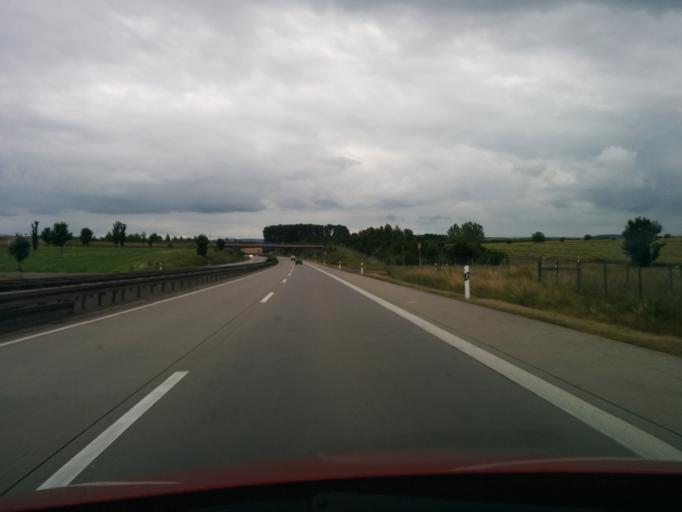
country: DE
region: Thuringia
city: Ingersleben
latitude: 50.9054
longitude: 10.9442
